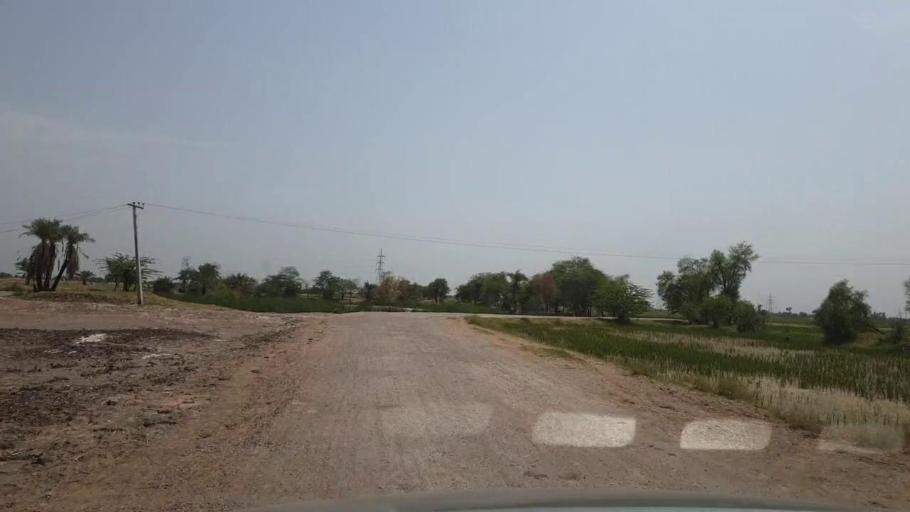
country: PK
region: Sindh
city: Garhi Yasin
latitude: 27.8946
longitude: 68.4711
